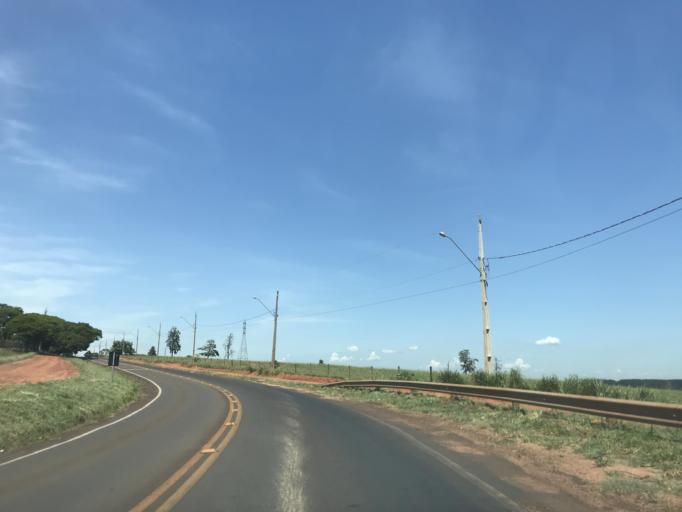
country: BR
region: Parana
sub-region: Paranavai
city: Nova Aurora
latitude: -22.9435
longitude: -52.6959
